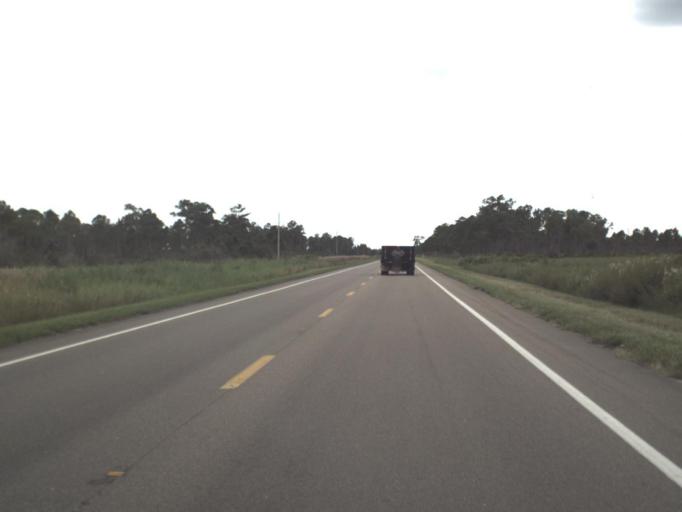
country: US
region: Florida
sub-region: Lee County
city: Olga
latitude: 26.8453
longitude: -81.7598
